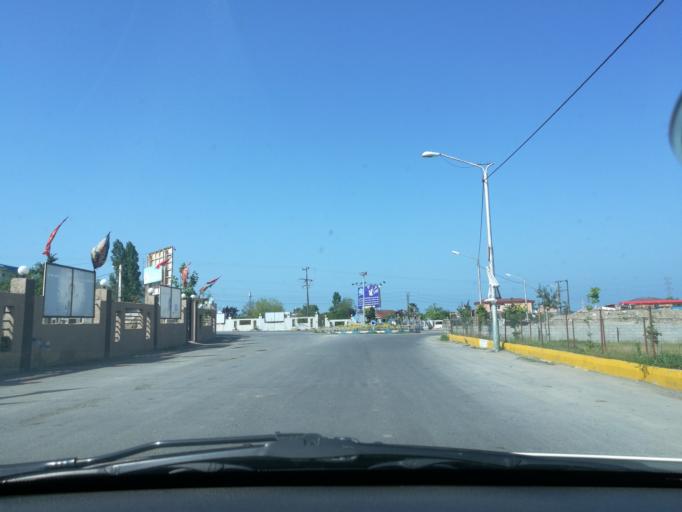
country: IR
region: Mazandaran
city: Chalus
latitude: 36.6585
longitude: 51.4330
